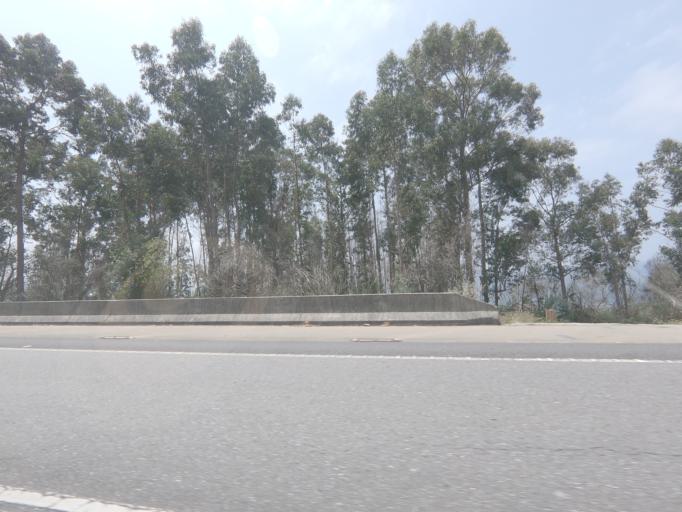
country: ES
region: Galicia
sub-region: Provincia de Pontevedra
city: A Guarda
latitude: 41.9249
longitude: -8.8809
